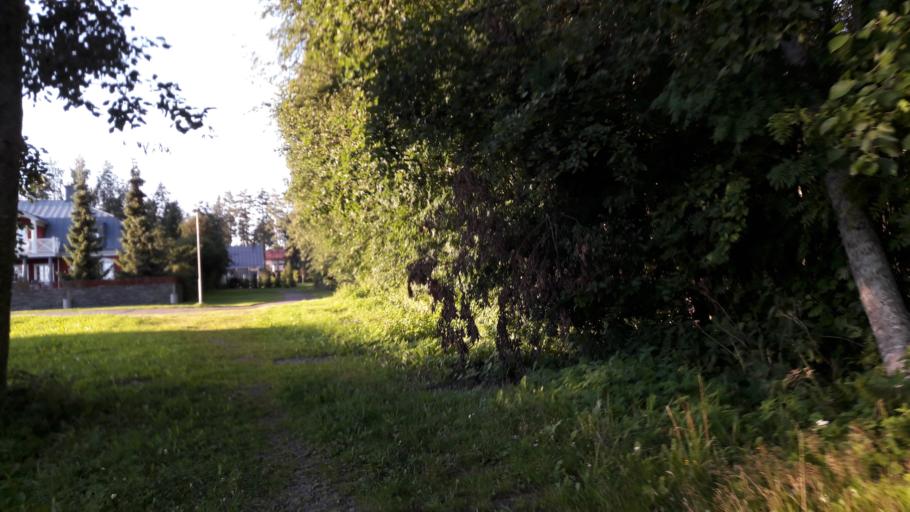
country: FI
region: North Karelia
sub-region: Joensuu
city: Joensuu
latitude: 62.6131
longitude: 29.7156
